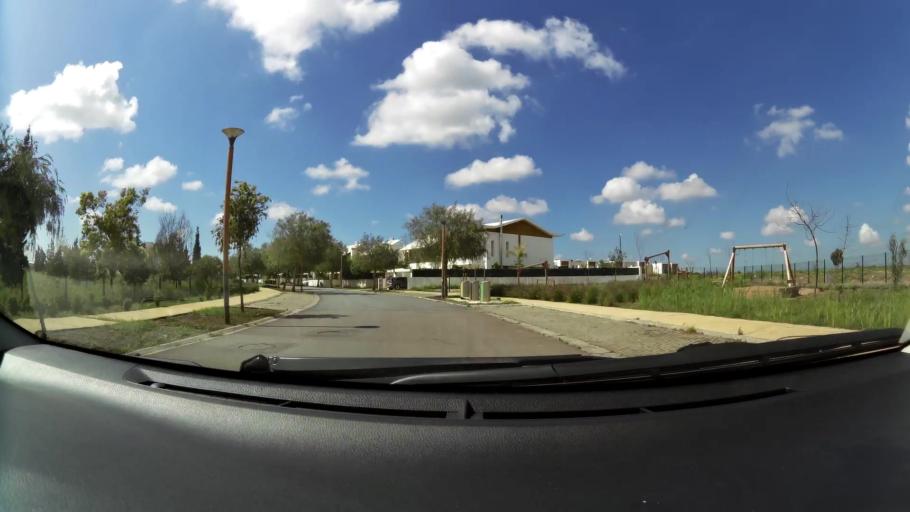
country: MA
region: Grand Casablanca
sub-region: Mediouna
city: Mediouna
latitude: 33.4863
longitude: -7.5796
